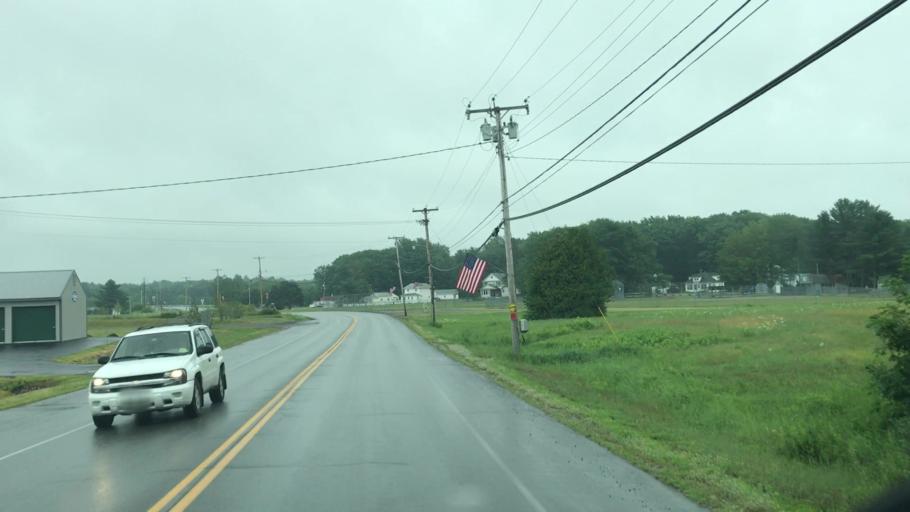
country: US
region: Maine
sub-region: Penobscot County
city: Howland
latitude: 45.2371
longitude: -68.6592
